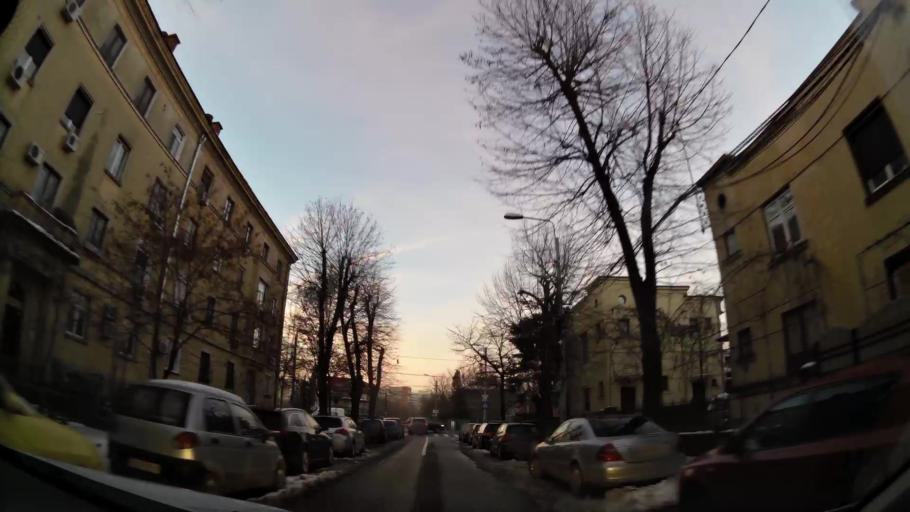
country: RO
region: Ilfov
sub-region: Comuna Fundeni-Dobroesti
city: Fundeni
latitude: 44.4384
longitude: 26.1415
